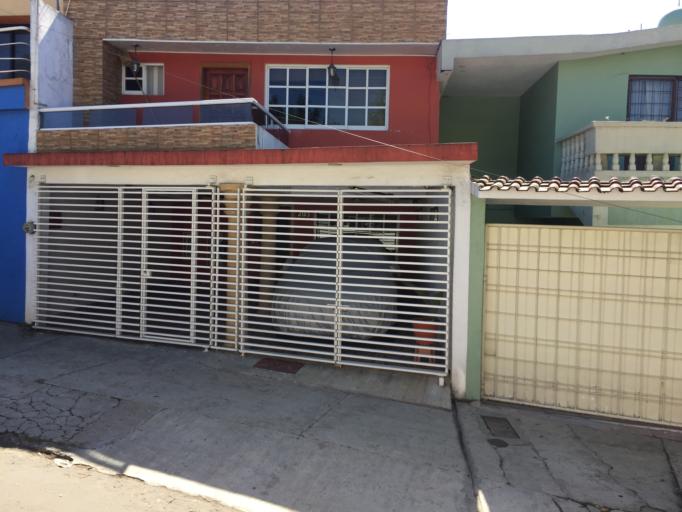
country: MX
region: Veracruz
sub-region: Xalapa
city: Xalapa de Enriquez
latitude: 19.5490
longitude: -96.9351
